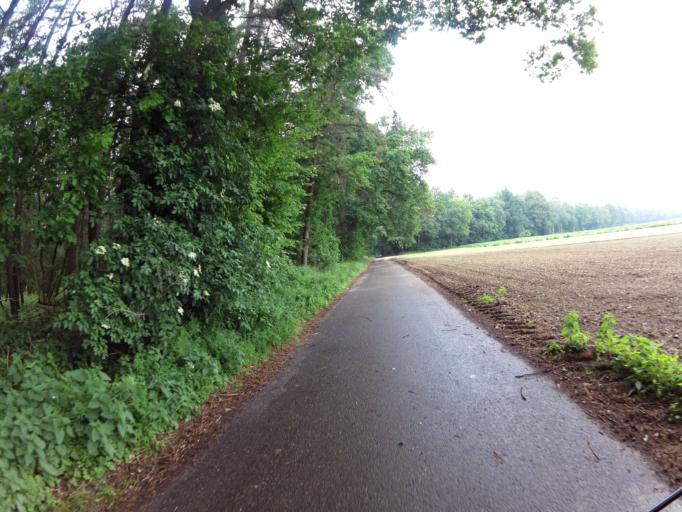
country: DE
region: North Rhine-Westphalia
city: Geilenkirchen
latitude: 50.9974
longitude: 6.1142
